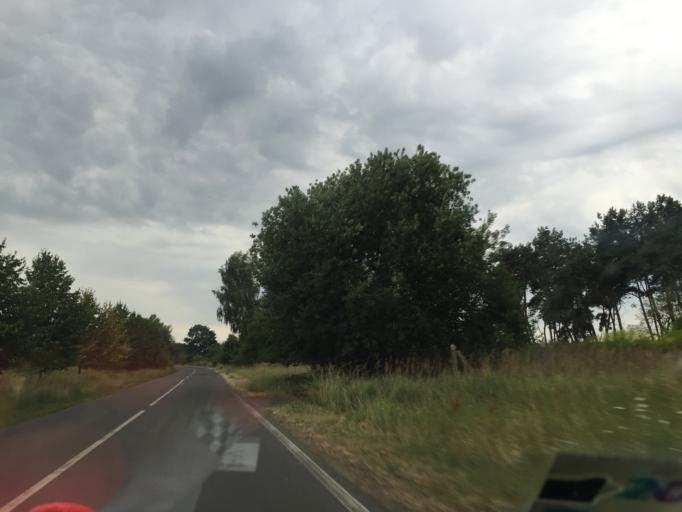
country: DE
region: Brandenburg
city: Zehdenick
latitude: 53.0181
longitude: 13.2868
